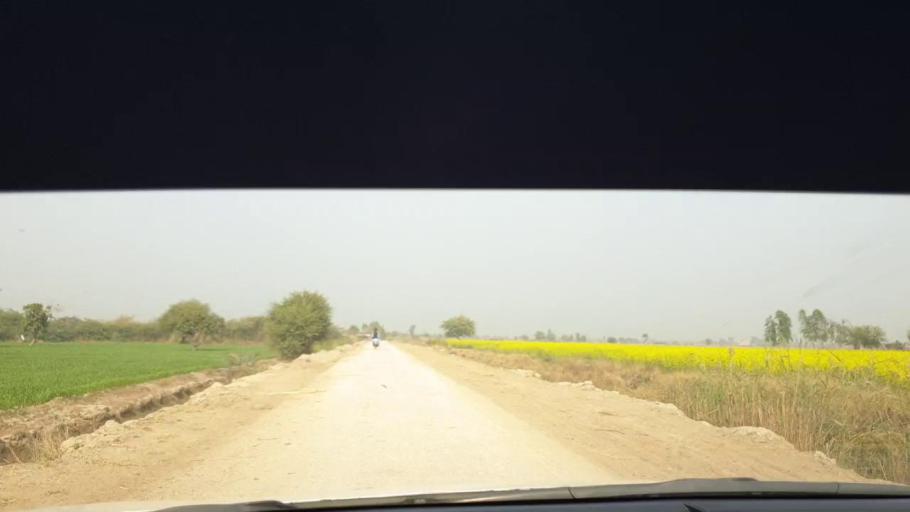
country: PK
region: Sindh
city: Berani
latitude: 25.8165
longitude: 68.8434
